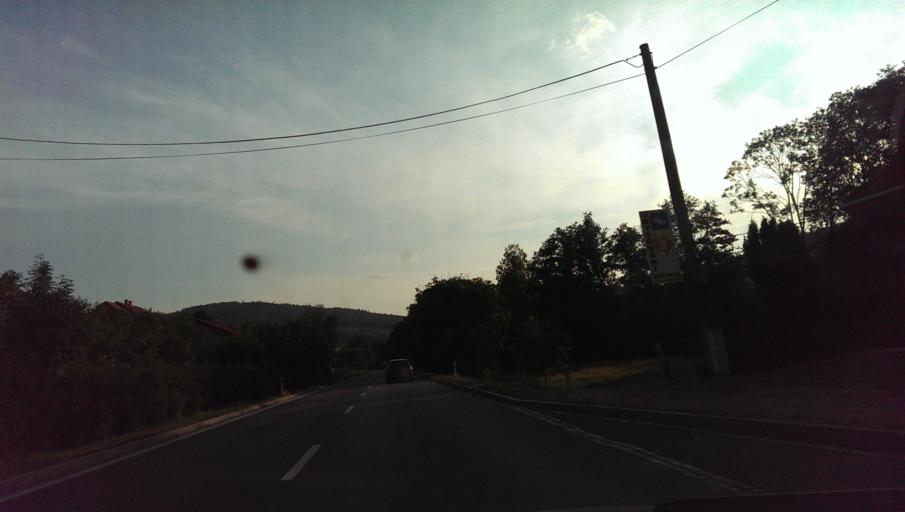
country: CZ
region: Zlin
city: Pozlovice
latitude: 49.1313
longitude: 17.8051
